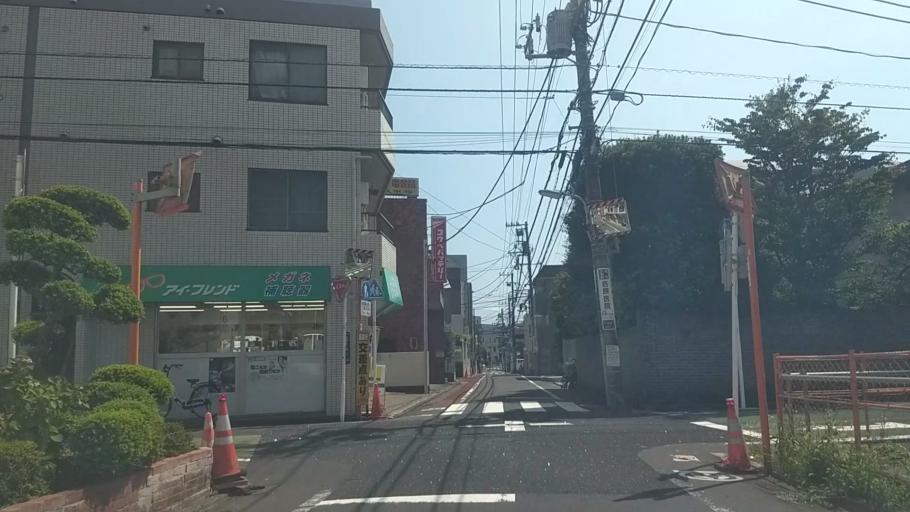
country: JP
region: Tokyo
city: Tokyo
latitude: 35.6089
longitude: 139.7197
